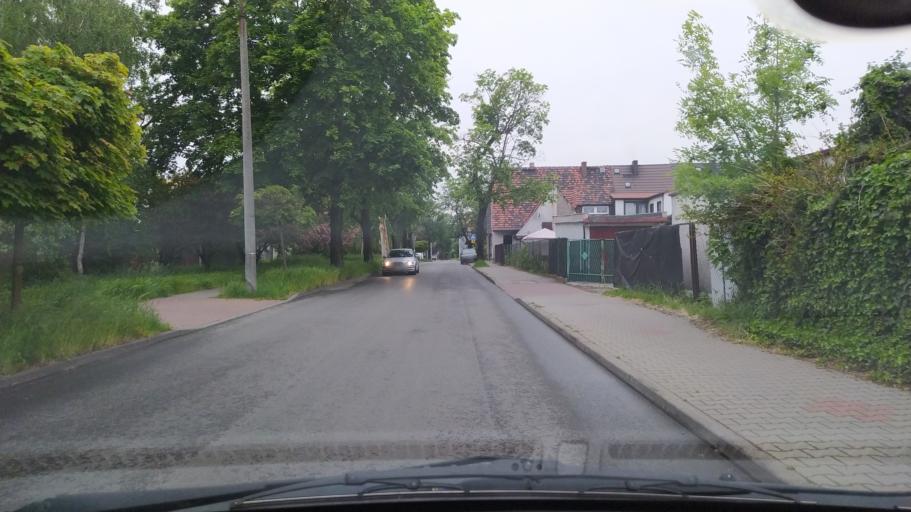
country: PL
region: Silesian Voivodeship
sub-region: Powiat gliwicki
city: Przyszowice
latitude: 50.2929
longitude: 18.7389
